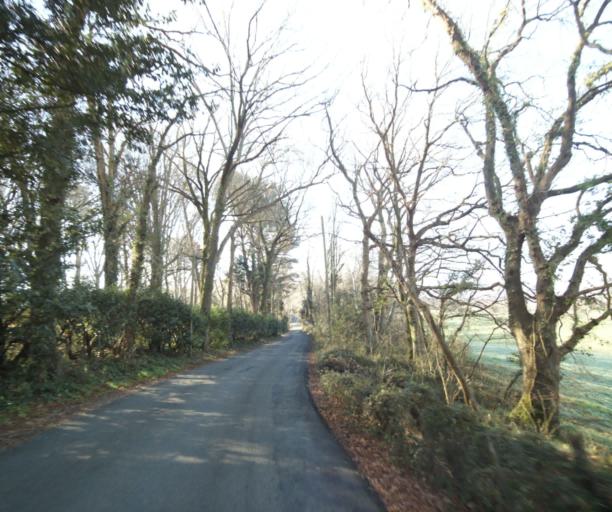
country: FR
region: Aquitaine
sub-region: Departement des Pyrenees-Atlantiques
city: Ciboure
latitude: 43.3649
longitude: -1.6607
